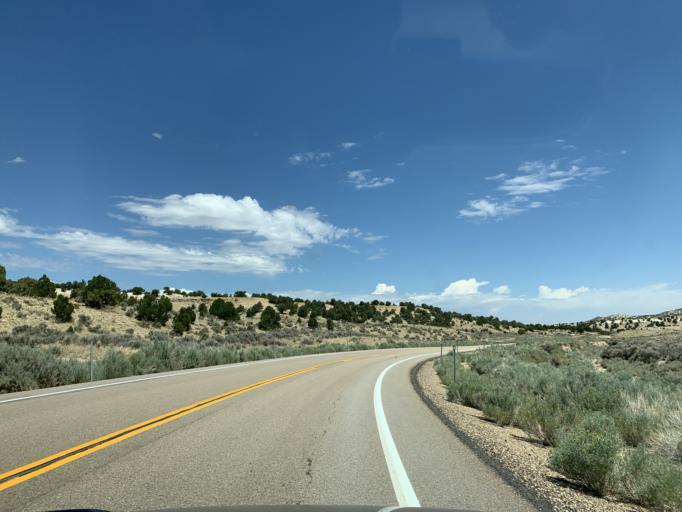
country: US
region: Utah
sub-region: Duchesne County
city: Duchesne
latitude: 39.9024
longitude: -110.2356
